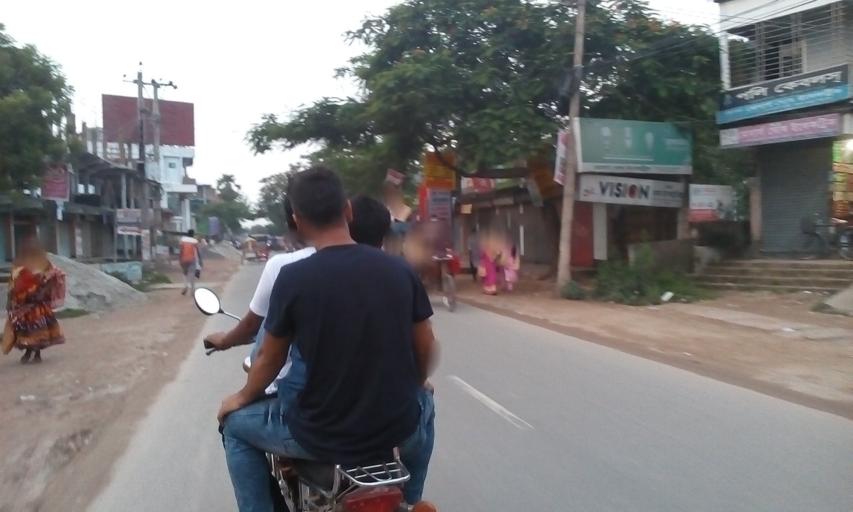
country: IN
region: West Bengal
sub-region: Dakshin Dinajpur
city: Balurghat
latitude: 25.3873
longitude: 88.9883
